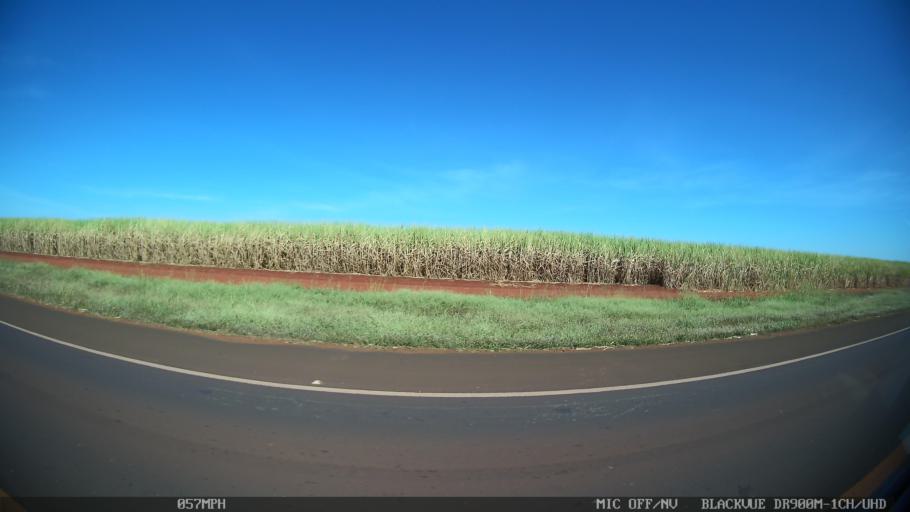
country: BR
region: Sao Paulo
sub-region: Guaira
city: Guaira
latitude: -20.4446
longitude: -48.2684
